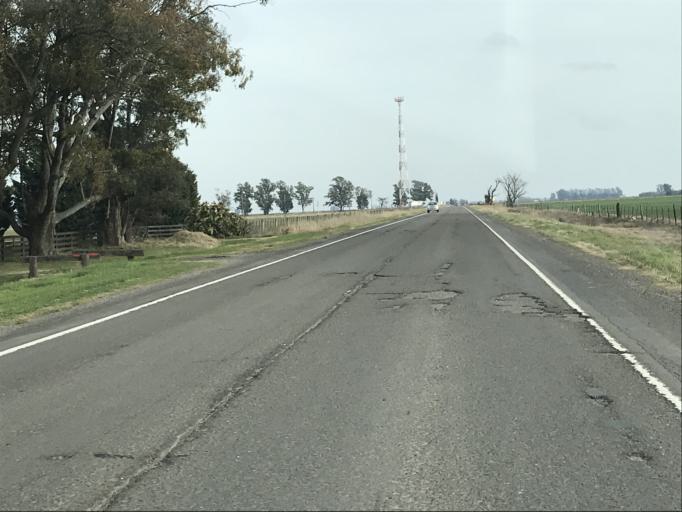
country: AR
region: Santa Fe
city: Armstrong
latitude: -32.7668
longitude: -61.6472
